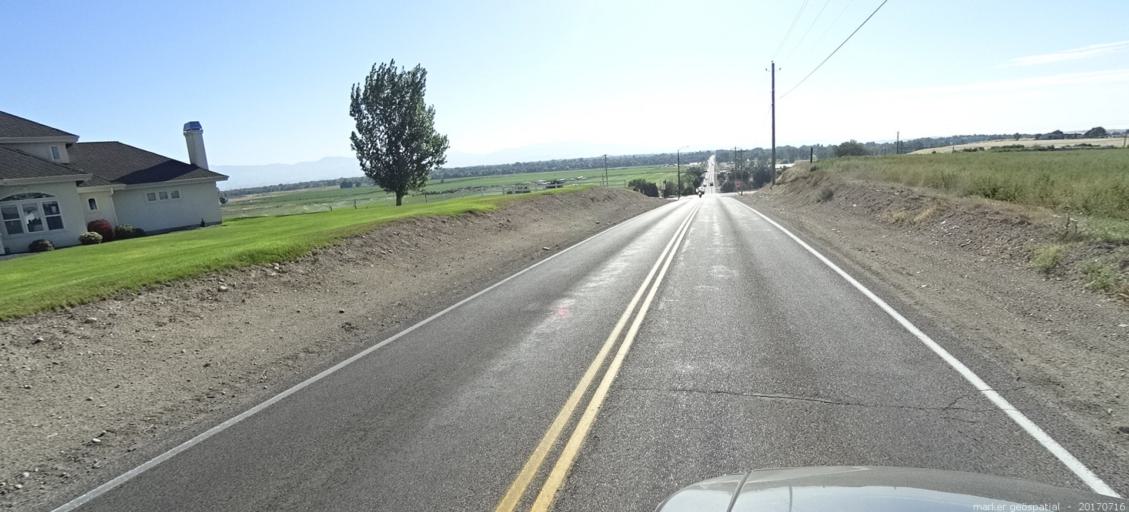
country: US
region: Idaho
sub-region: Ada County
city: Meridian
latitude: 43.5465
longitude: -116.3562
